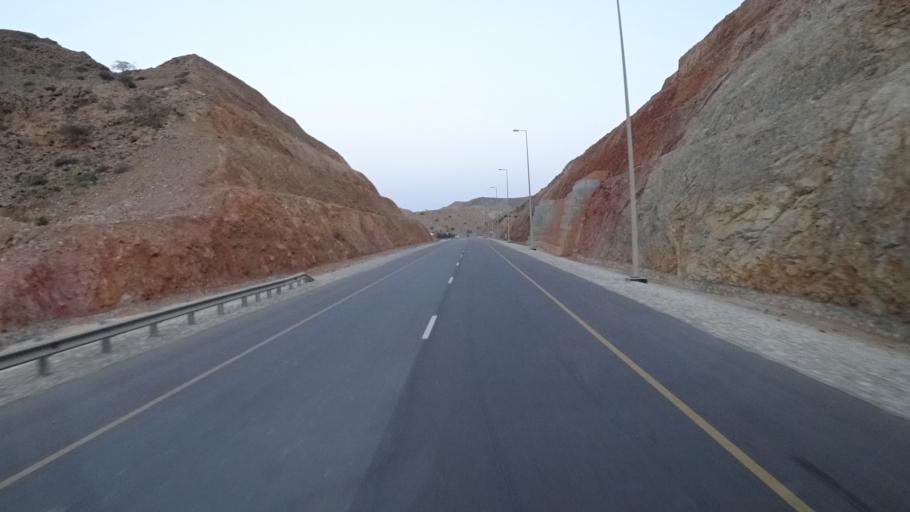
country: OM
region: Muhafazat Masqat
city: Muscat
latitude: 23.5085
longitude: 58.7250
